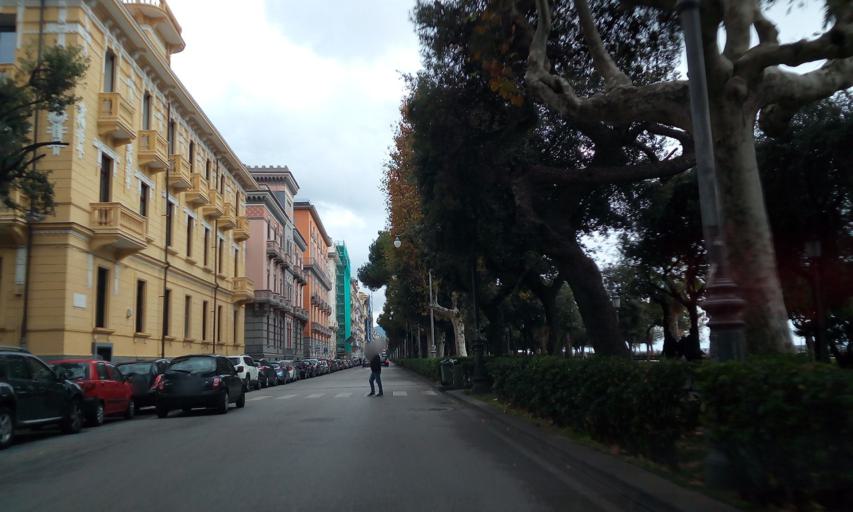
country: IT
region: Campania
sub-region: Provincia di Salerno
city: Capezzano Inferiore
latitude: 40.6776
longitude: 14.7598
